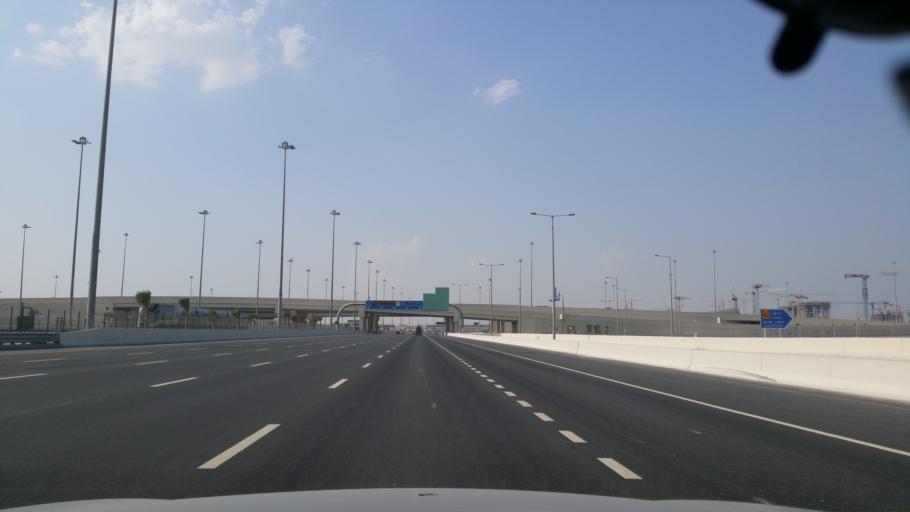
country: QA
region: Baladiyat Umm Salal
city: Umm Salal Muhammad
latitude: 25.4015
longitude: 51.4930
